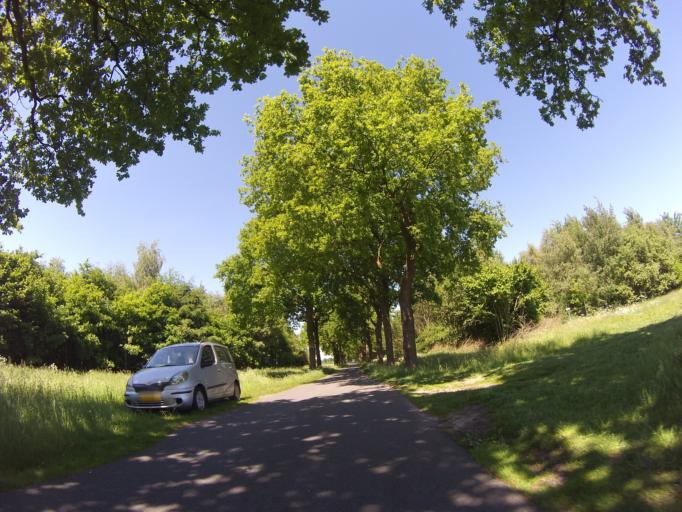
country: NL
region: Drenthe
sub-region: Gemeente Hoogeveen
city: Hoogeveen
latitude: 52.7772
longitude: 6.5164
